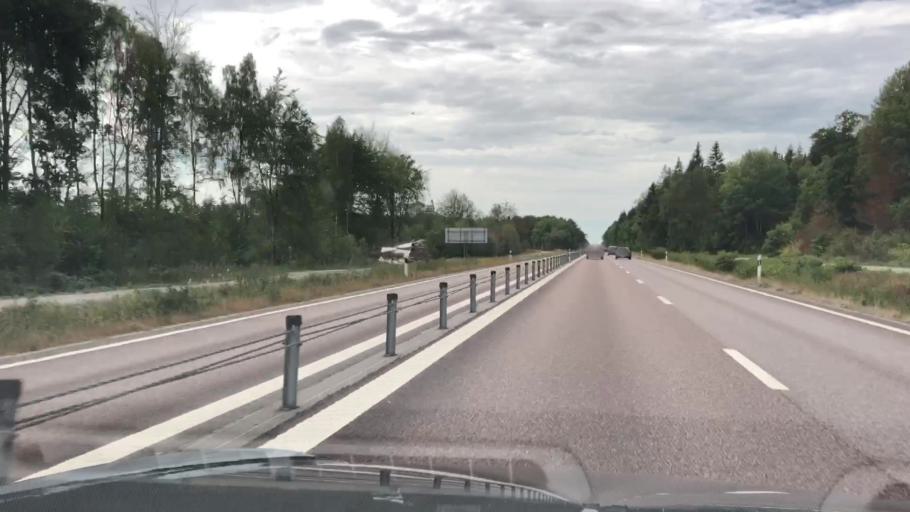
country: SE
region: Blekinge
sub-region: Karlskrona Kommun
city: Jaemjoe
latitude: 56.2225
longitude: 15.9024
